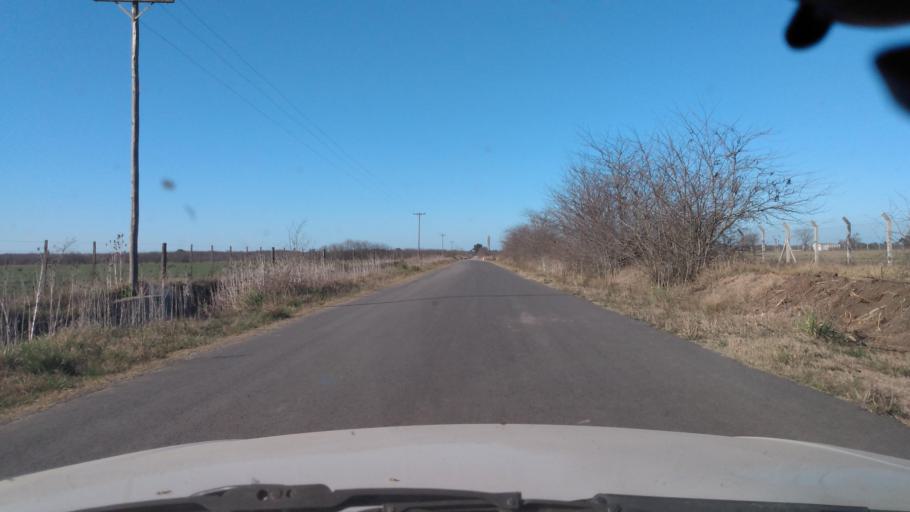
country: AR
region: Buenos Aires
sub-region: Partido de Mercedes
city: Mercedes
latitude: -34.6186
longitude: -59.3386
